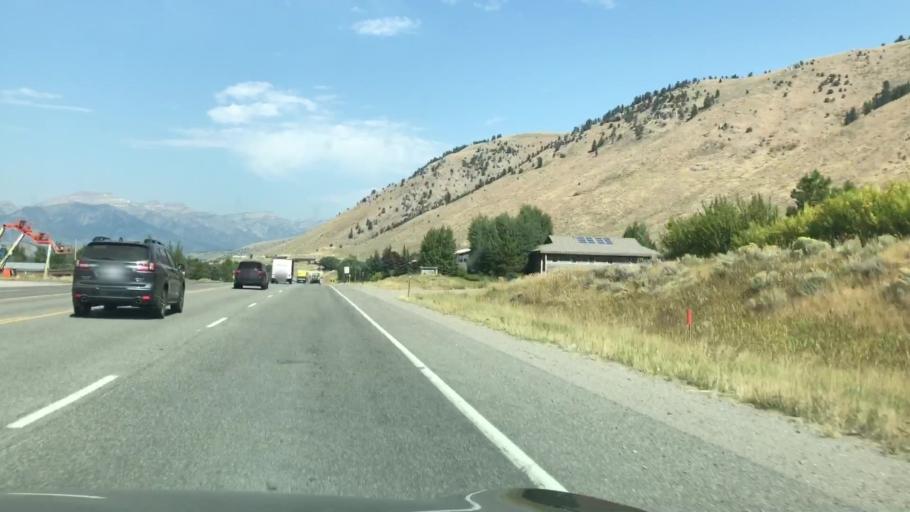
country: US
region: Wyoming
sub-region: Teton County
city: South Park
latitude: 43.4200
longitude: -110.7754
